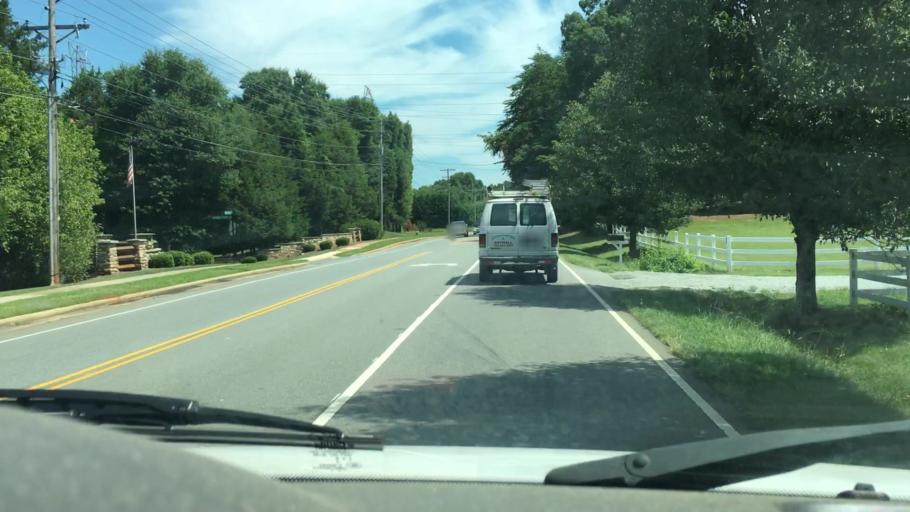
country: US
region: North Carolina
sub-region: Mecklenburg County
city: Huntersville
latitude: 35.4138
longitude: -80.9239
